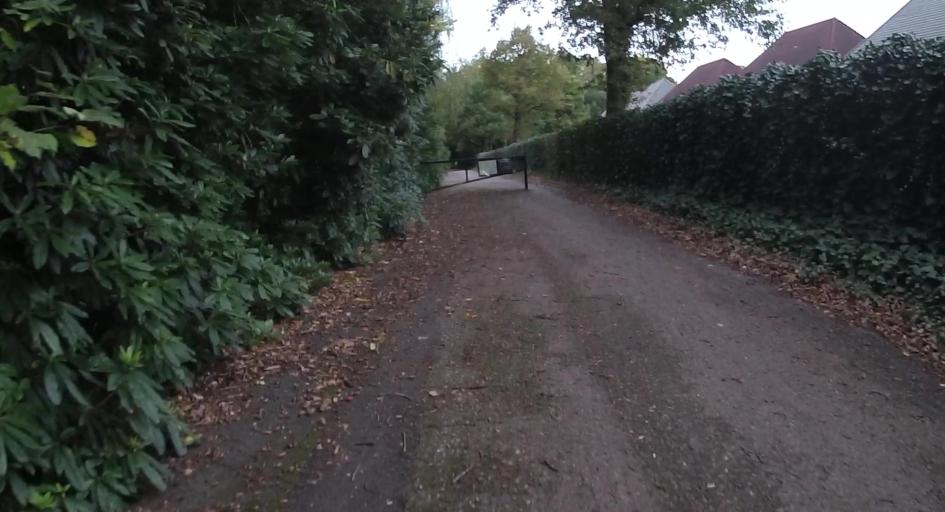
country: GB
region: England
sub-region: Bracknell Forest
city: Crowthorne
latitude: 51.3999
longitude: -0.7847
